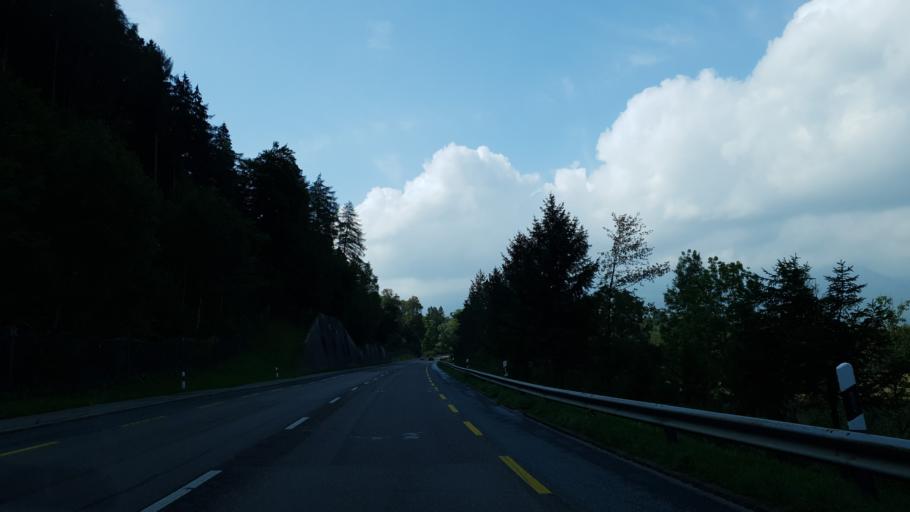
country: LI
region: Planken
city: Planken
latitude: 47.1884
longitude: 9.5389
